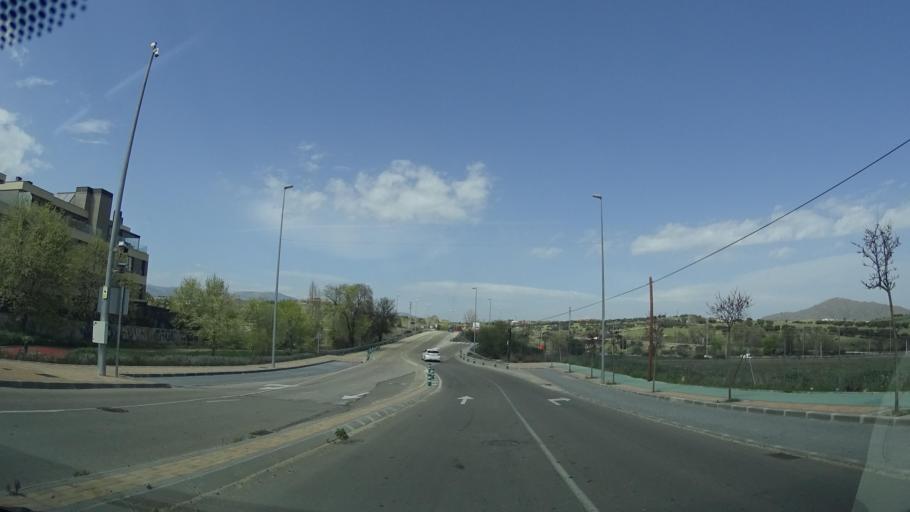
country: ES
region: Madrid
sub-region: Provincia de Madrid
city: Colmenar Viejo
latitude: 40.6780
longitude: -3.7694
